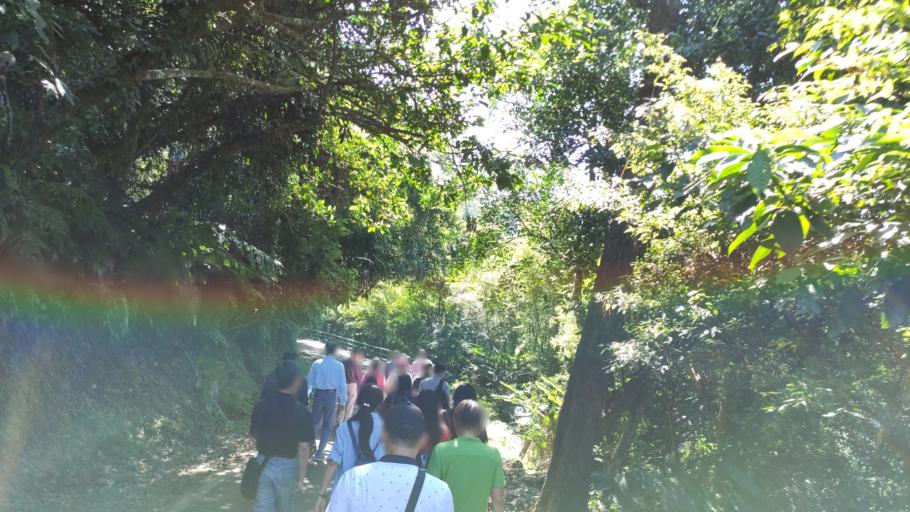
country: TW
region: Taiwan
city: Daxi
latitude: 24.8397
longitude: 121.3071
